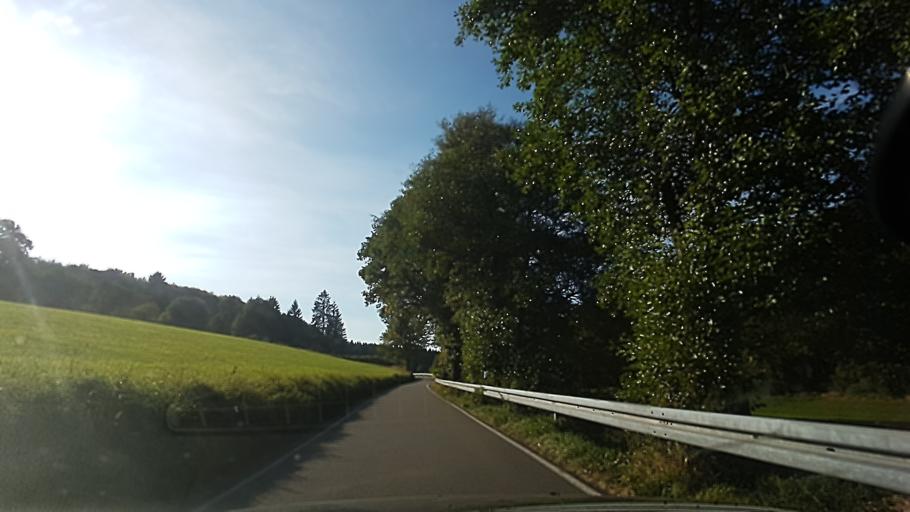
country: DE
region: North Rhine-Westphalia
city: Kierspe
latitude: 51.1448
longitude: 7.5640
